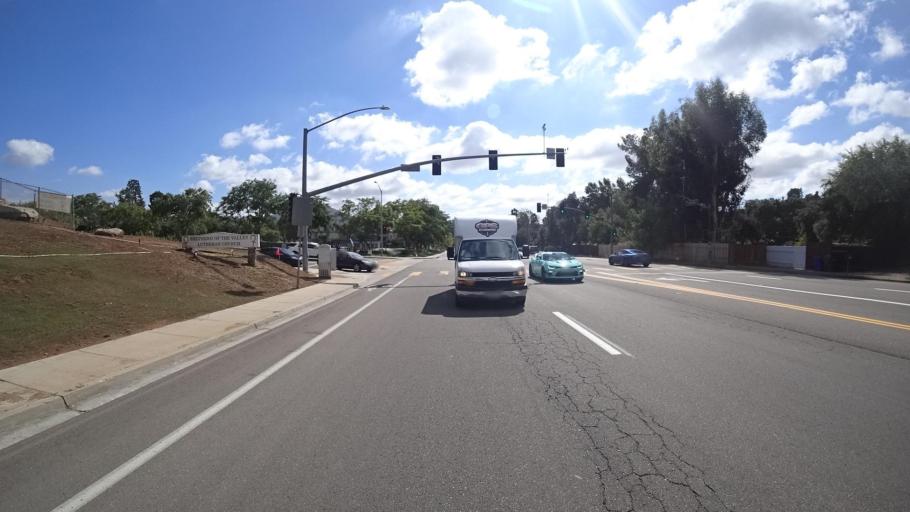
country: US
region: California
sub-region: San Diego County
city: Casa de Oro-Mount Helix
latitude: 32.7517
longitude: -116.9619
